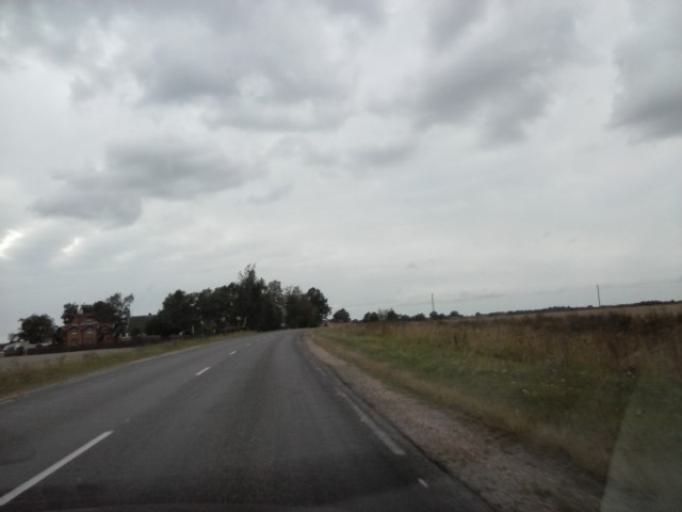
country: LV
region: Rundales
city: Pilsrundale
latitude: 56.4191
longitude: 23.7797
